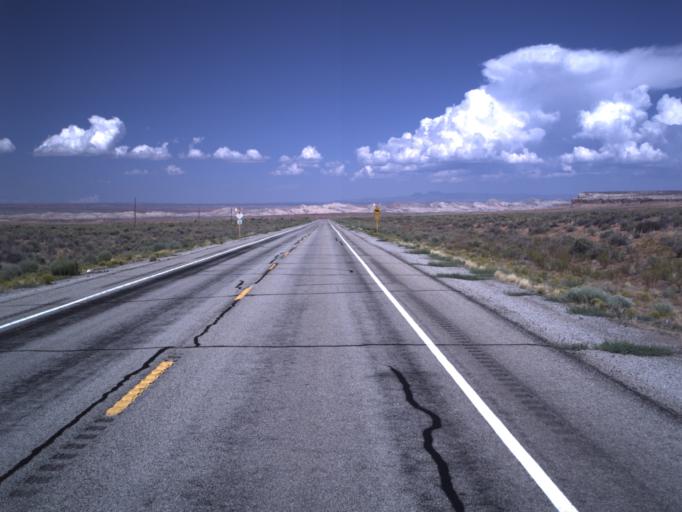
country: US
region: Utah
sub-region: San Juan County
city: Blanding
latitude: 37.1864
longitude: -109.5926
